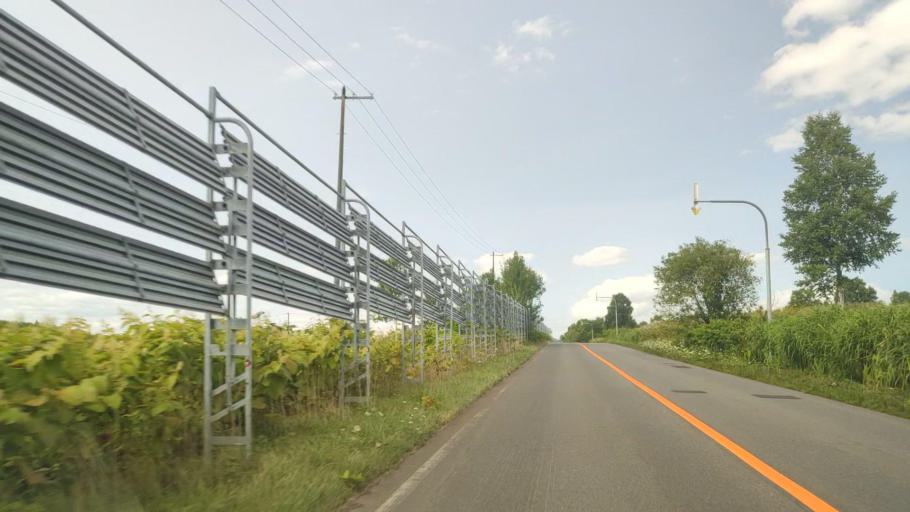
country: JP
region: Hokkaido
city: Nayoro
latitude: 44.2464
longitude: 142.4156
